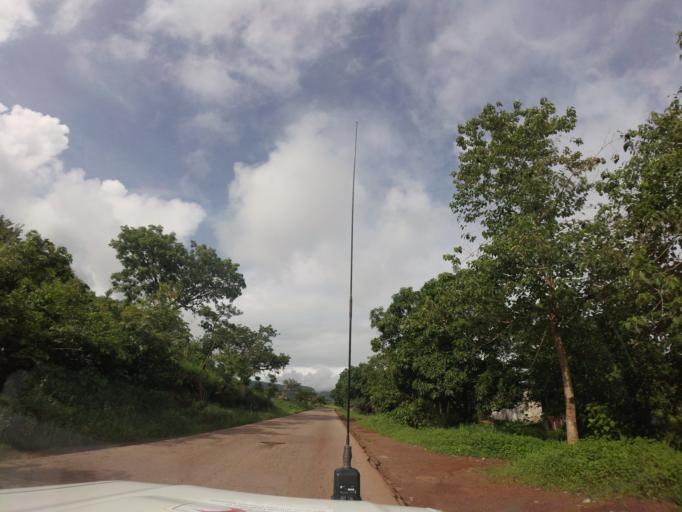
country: GN
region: Kindia
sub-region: Coyah
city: Coyah
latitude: 9.8241
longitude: -13.2597
